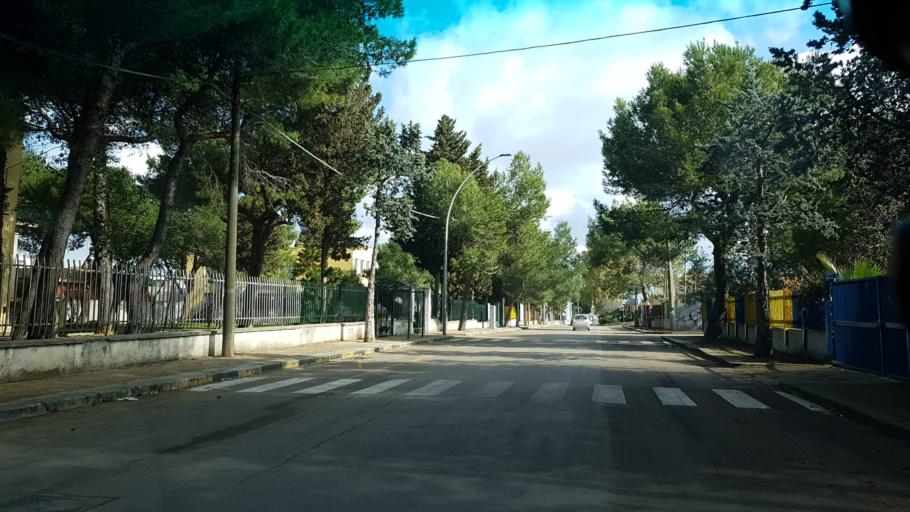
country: IT
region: Apulia
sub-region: Provincia di Brindisi
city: San Pietro Vernotico
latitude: 40.4810
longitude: 18.0011
